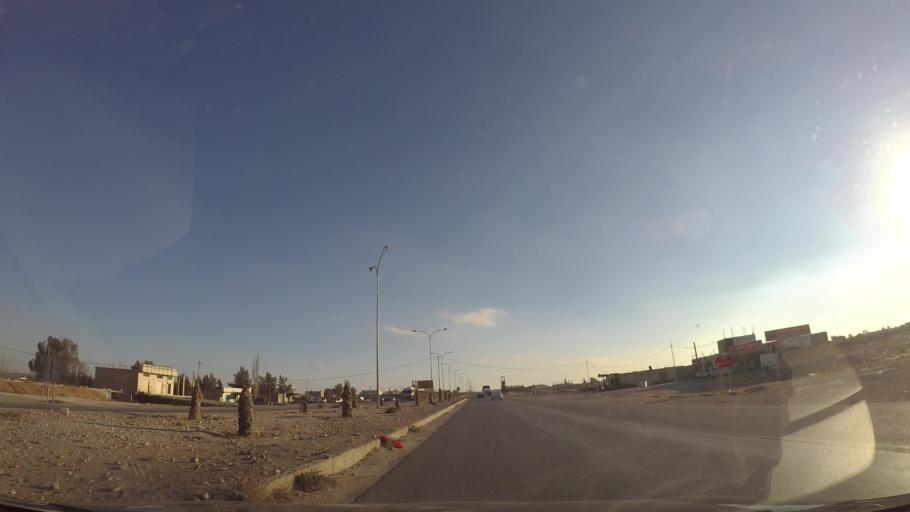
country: JO
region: Tafielah
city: Busayra
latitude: 30.5932
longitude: 35.8031
